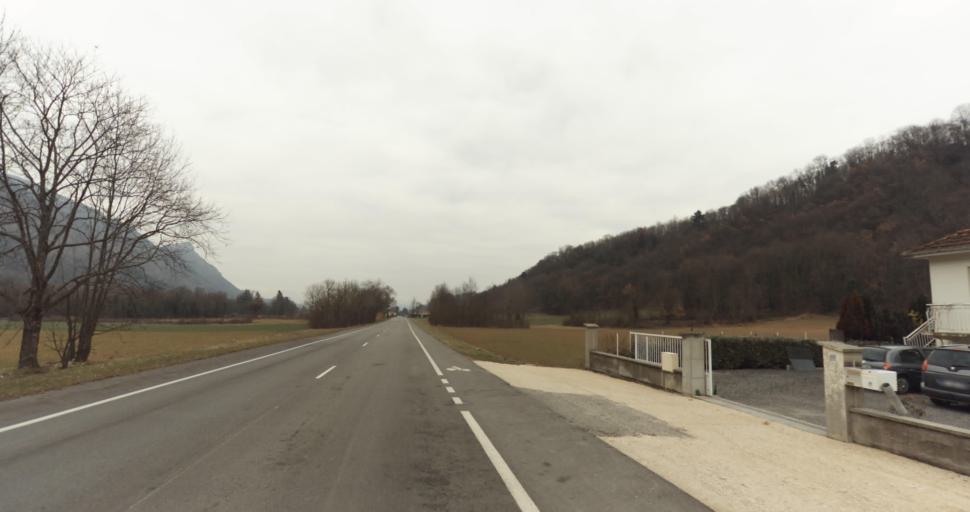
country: FR
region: Rhone-Alpes
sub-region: Departement de l'Isere
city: Vif
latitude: 45.0344
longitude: 5.6573
